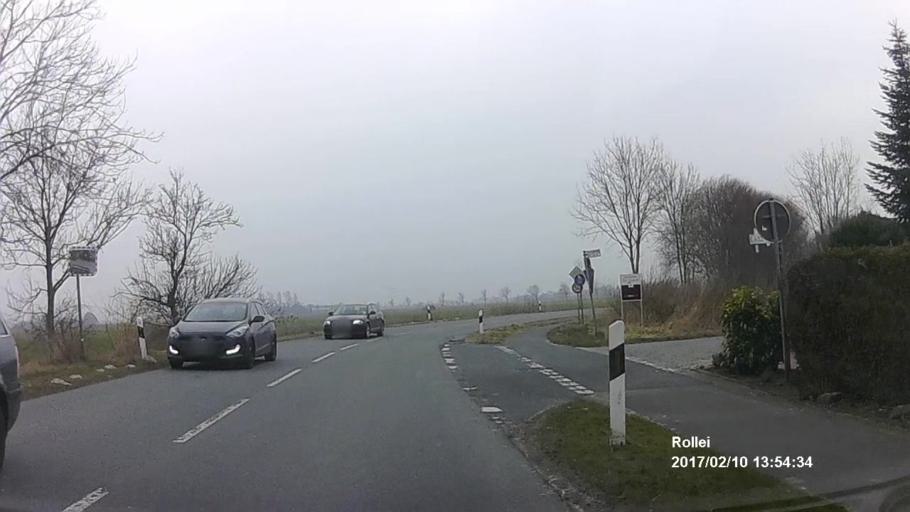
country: DE
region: Lower Saxony
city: Norddeich
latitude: 53.5657
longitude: 7.1399
